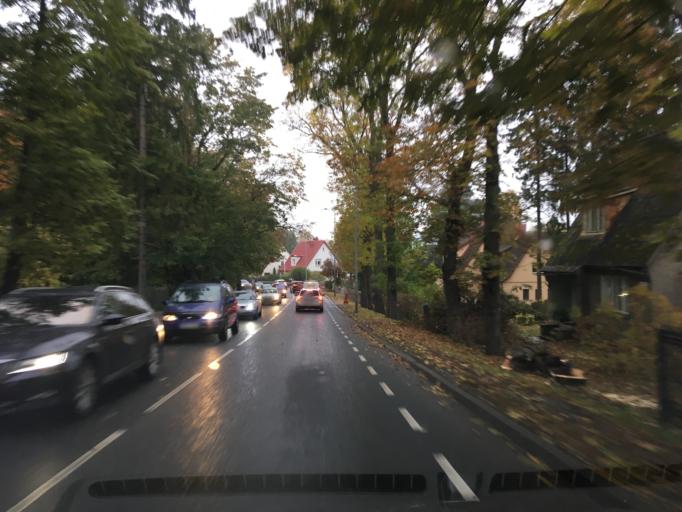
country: EE
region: Harju
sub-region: Tallinna linn
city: Kose
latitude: 59.4559
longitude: 24.8690
